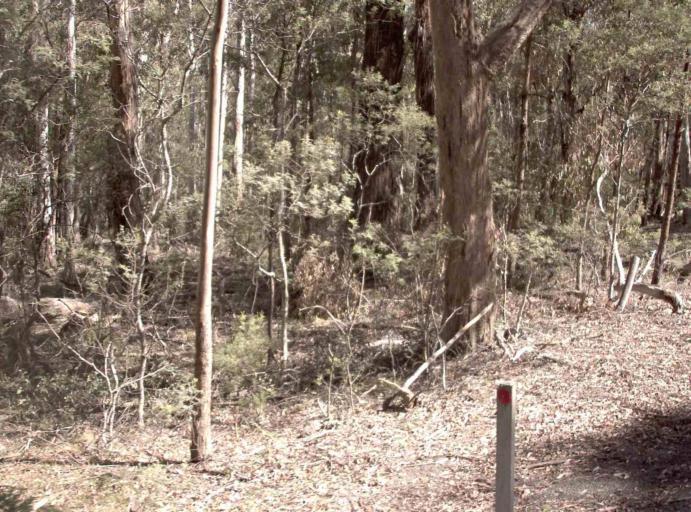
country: AU
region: New South Wales
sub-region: Bombala
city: Bombala
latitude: -37.1197
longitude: 148.7522
